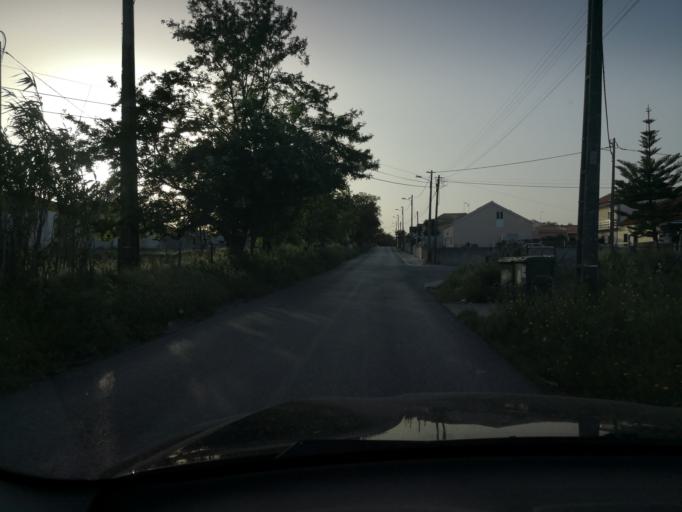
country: PT
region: Setubal
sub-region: Setubal
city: Setubal
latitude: 38.5311
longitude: -8.8118
